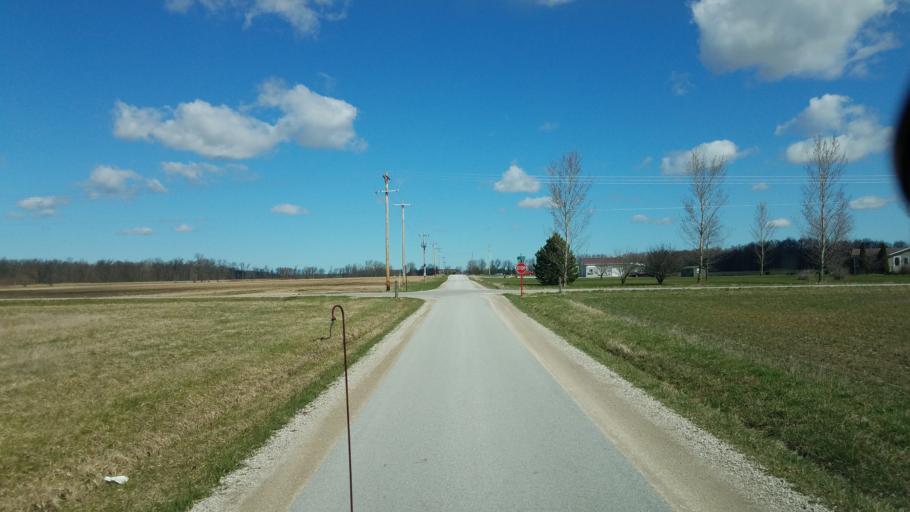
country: US
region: Ohio
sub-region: Sandusky County
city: Mount Carmel
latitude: 41.2116
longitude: -82.9373
